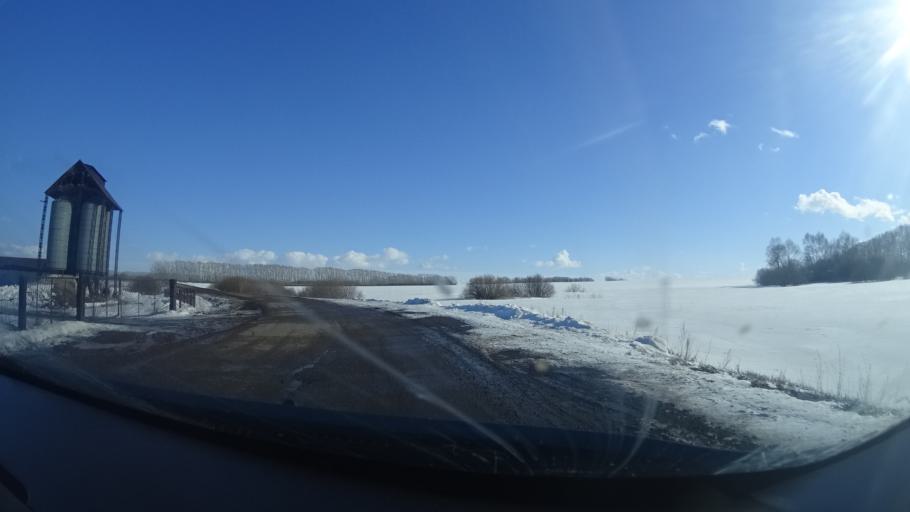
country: RU
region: Bashkortostan
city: Chishmy
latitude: 54.5891
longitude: 55.2576
